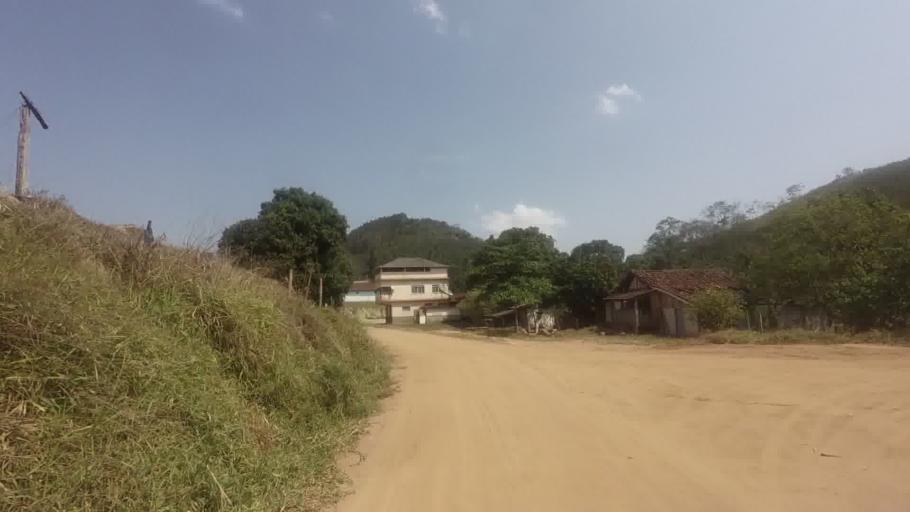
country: BR
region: Espirito Santo
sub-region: Mimoso Do Sul
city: Mimoso do Sul
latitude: -20.9969
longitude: -41.5028
